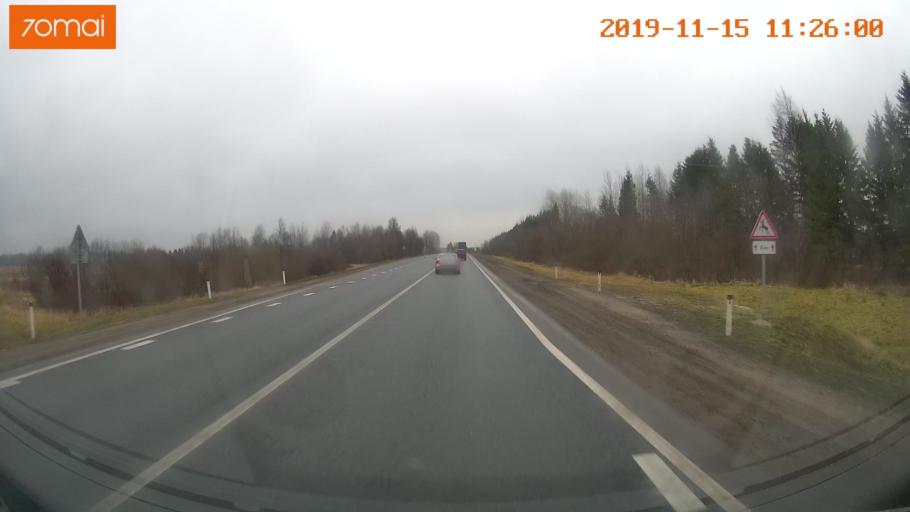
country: RU
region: Vologda
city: Molochnoye
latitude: 59.1649
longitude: 39.4367
